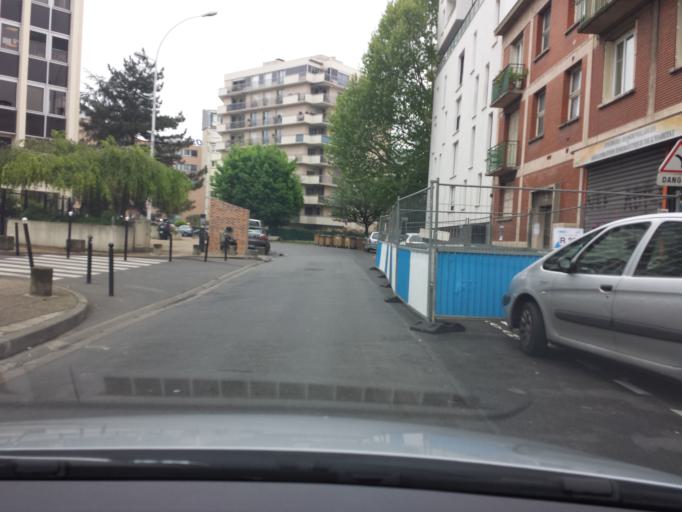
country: FR
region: Ile-de-France
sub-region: Departement du Val-de-Marne
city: Le Kremlin-Bicetre
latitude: 48.8154
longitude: 2.3529
